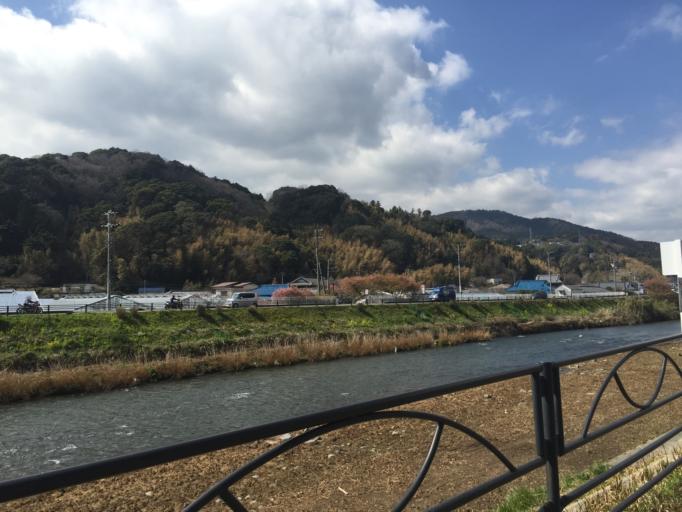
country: JP
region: Shizuoka
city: Shimoda
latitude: 34.7510
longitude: 138.9889
